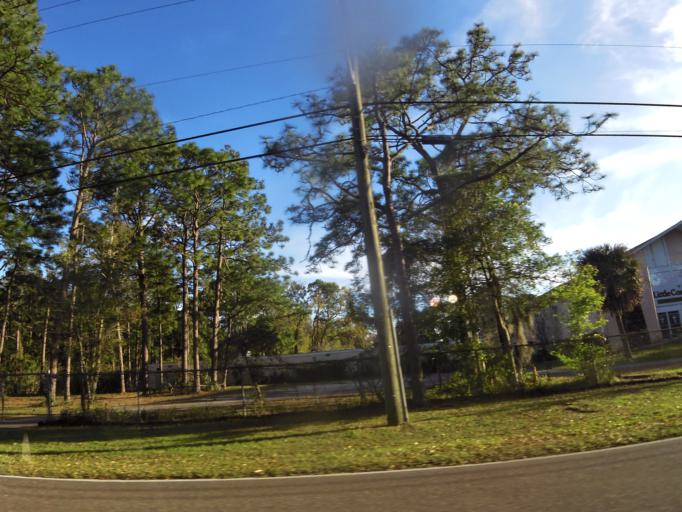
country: US
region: Florida
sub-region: Duval County
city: Jacksonville
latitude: 30.4397
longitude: -81.6216
